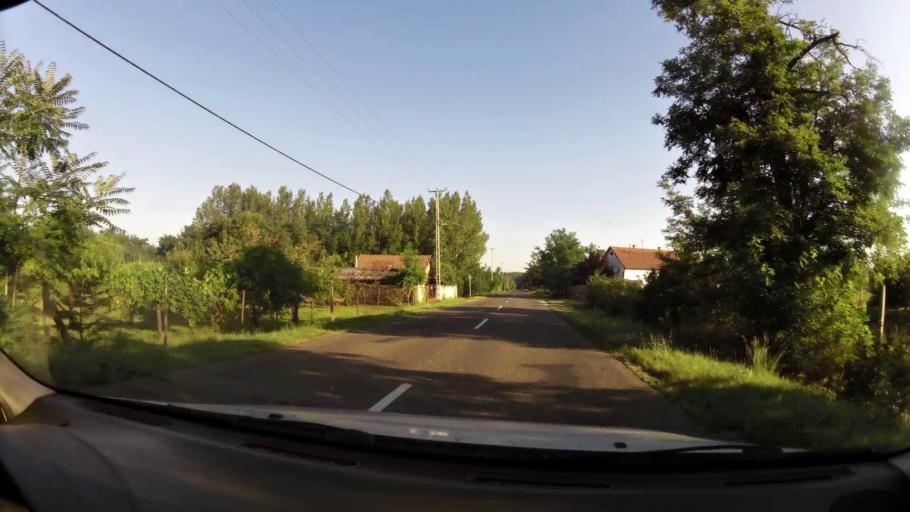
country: HU
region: Pest
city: Tapioszolos
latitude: 47.2761
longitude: 19.8818
